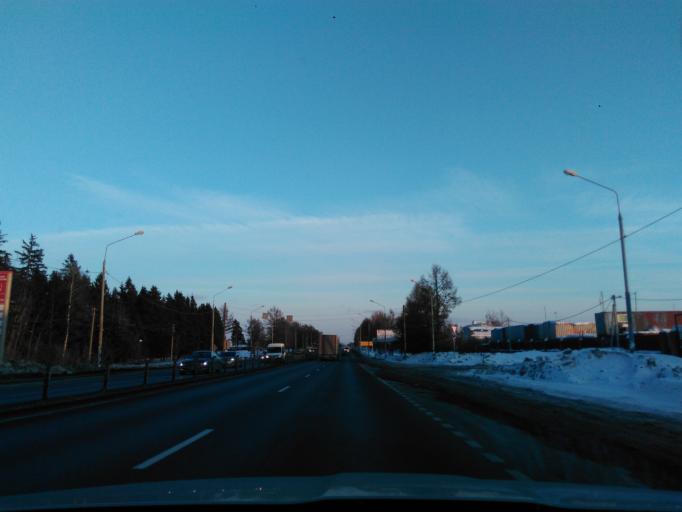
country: RU
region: Moskovskaya
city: Solnechnogorsk
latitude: 56.2374
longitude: 36.8971
